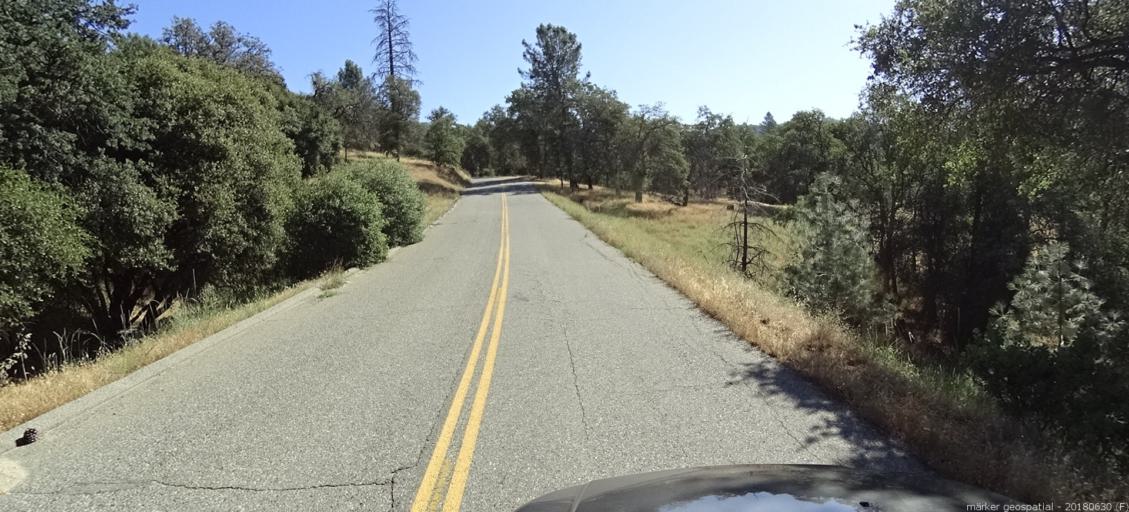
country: US
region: California
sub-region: Fresno County
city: Auberry
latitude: 37.1860
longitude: -119.4220
